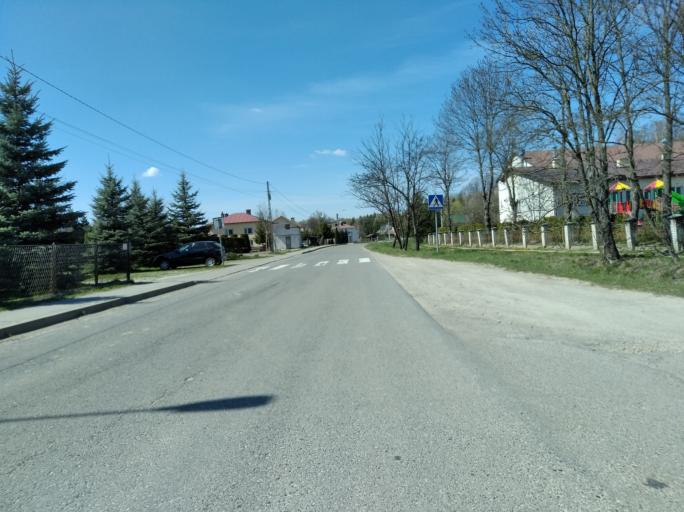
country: PL
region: Subcarpathian Voivodeship
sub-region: Powiat brzozowski
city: Golcowa
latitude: 49.7722
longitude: 22.0241
